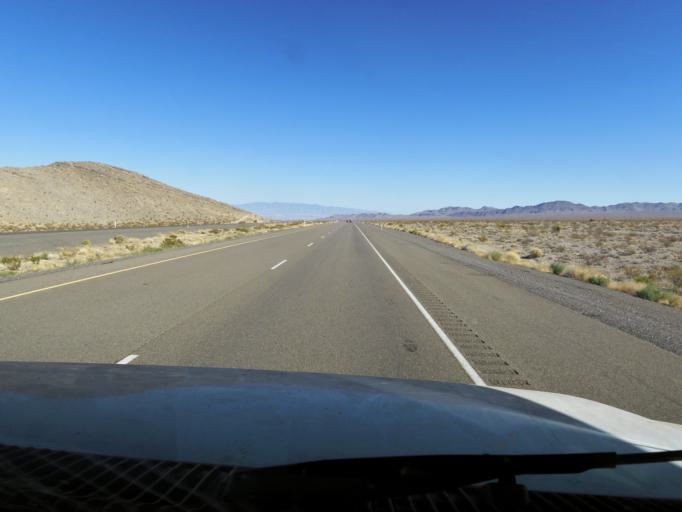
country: US
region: Nevada
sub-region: Nye County
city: Pahrump
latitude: 36.5708
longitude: -115.8600
